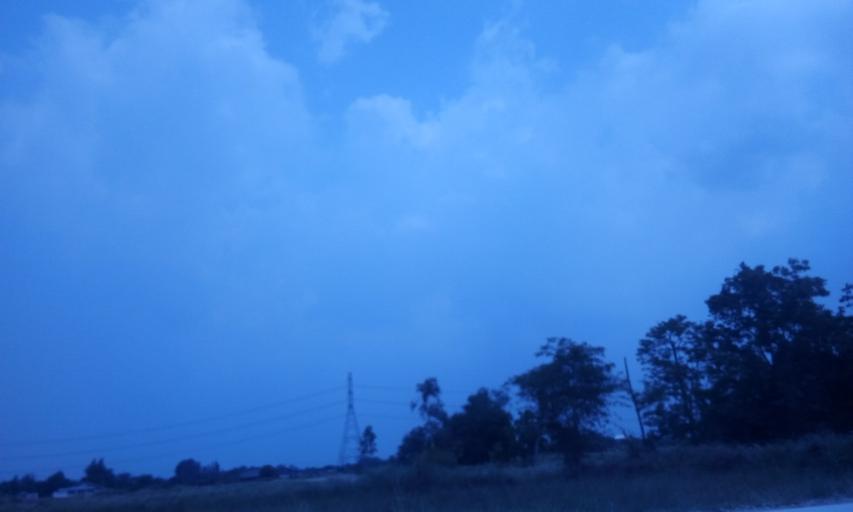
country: TH
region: Chon Buri
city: Ban Bueng
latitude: 13.3288
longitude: 101.1877
